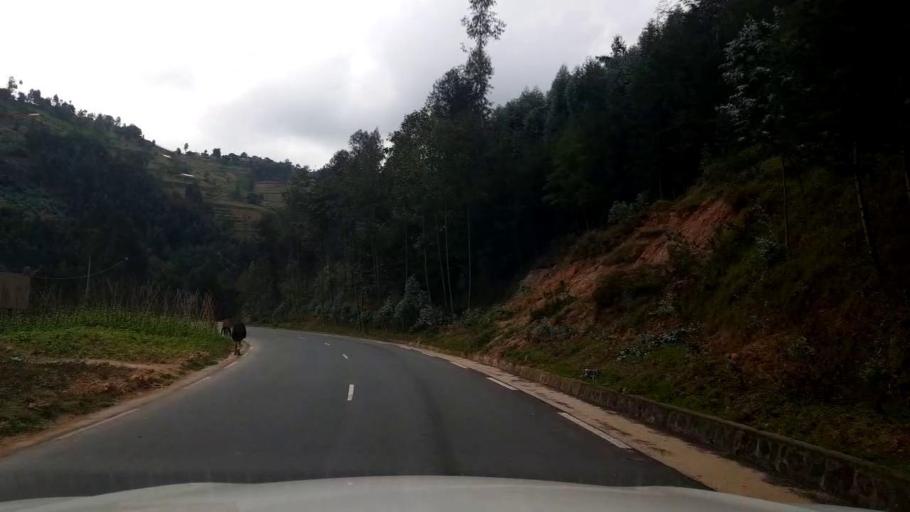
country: RW
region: Northern Province
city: Musanze
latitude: -1.6947
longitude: 29.5562
